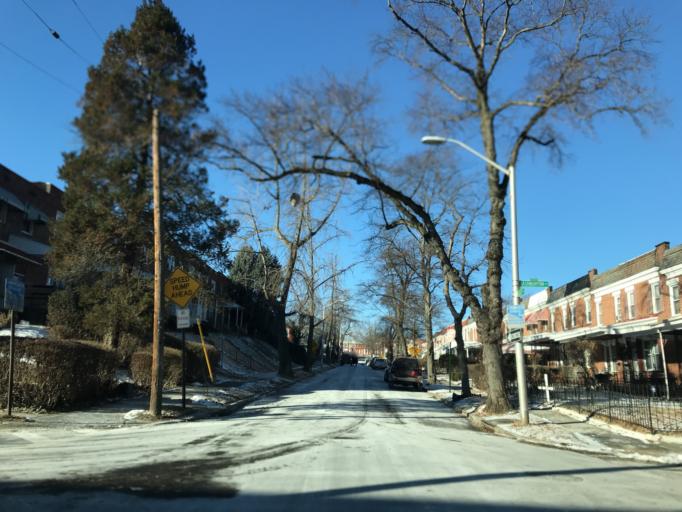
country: US
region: Maryland
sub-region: City of Baltimore
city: Baltimore
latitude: 39.3026
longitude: -76.6615
